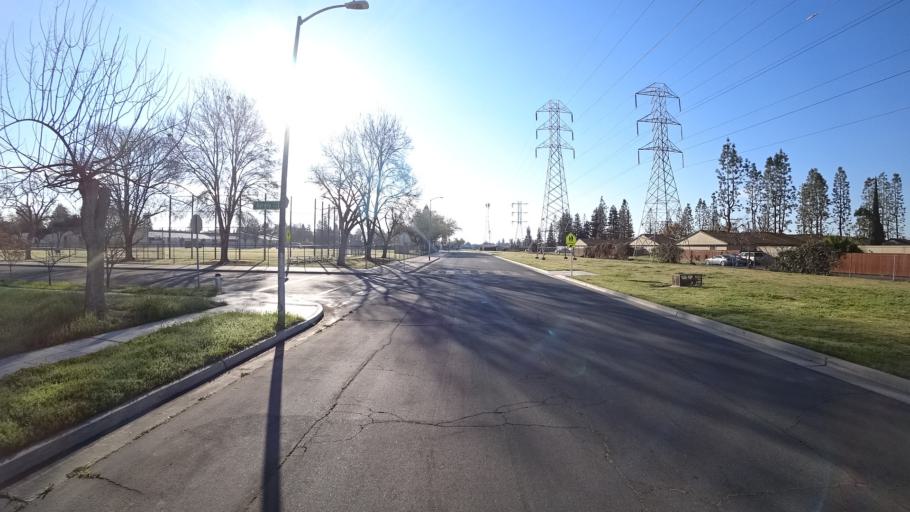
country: US
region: California
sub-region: Fresno County
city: West Park
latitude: 36.8134
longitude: -119.8696
